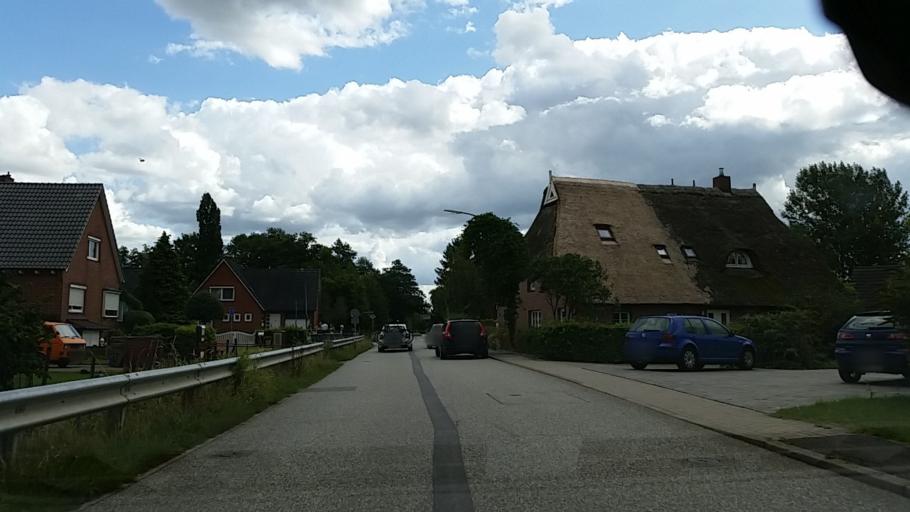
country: DE
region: Schleswig-Holstein
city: Bornsen
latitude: 53.4531
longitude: 10.2852
